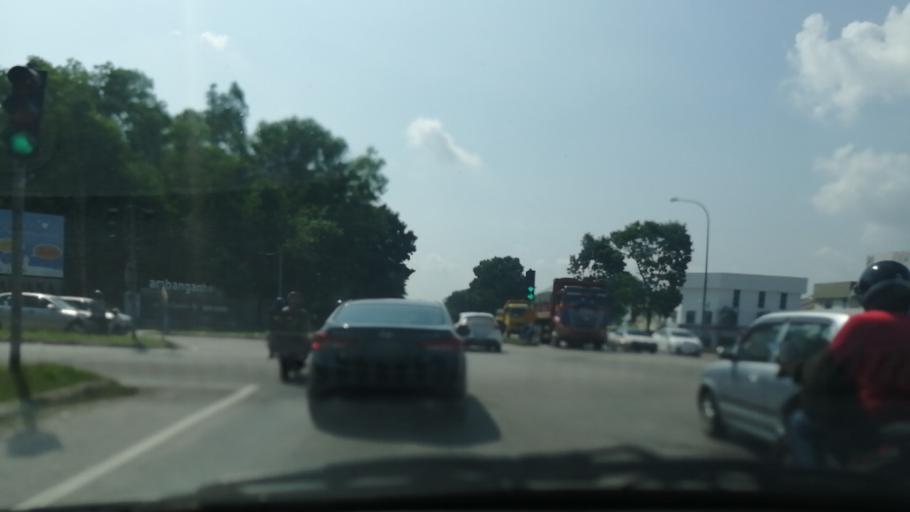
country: MY
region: Kedah
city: Sungai Petani
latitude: 5.6673
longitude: 100.5282
